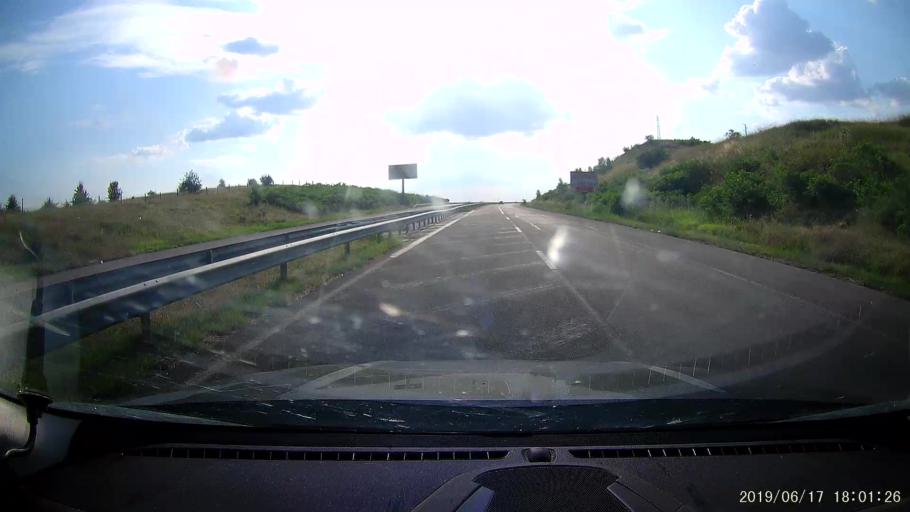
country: BG
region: Khaskovo
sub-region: Obshtina Svilengrad
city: Svilengrad
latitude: 41.7457
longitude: 26.2546
